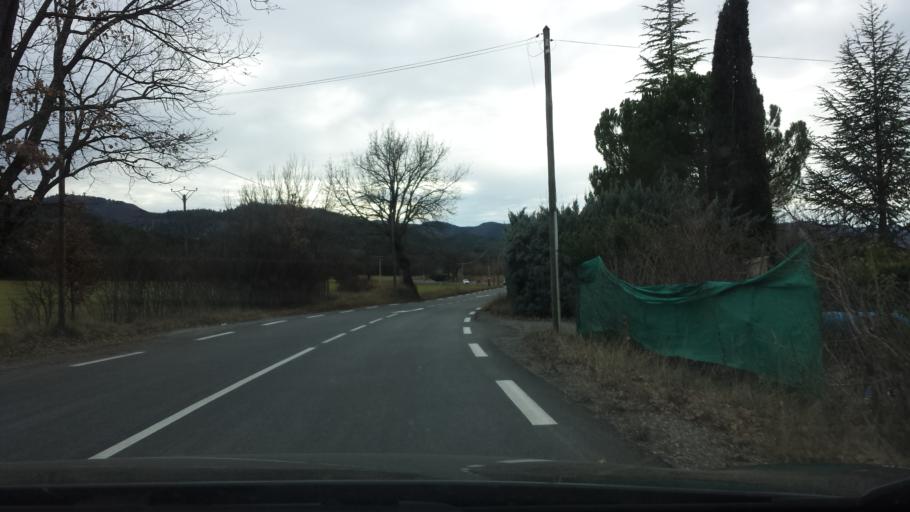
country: FR
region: Provence-Alpes-Cote d'Azur
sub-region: Departement des Alpes-de-Haute-Provence
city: Mallemoisson
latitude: 44.0468
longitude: 6.1621
